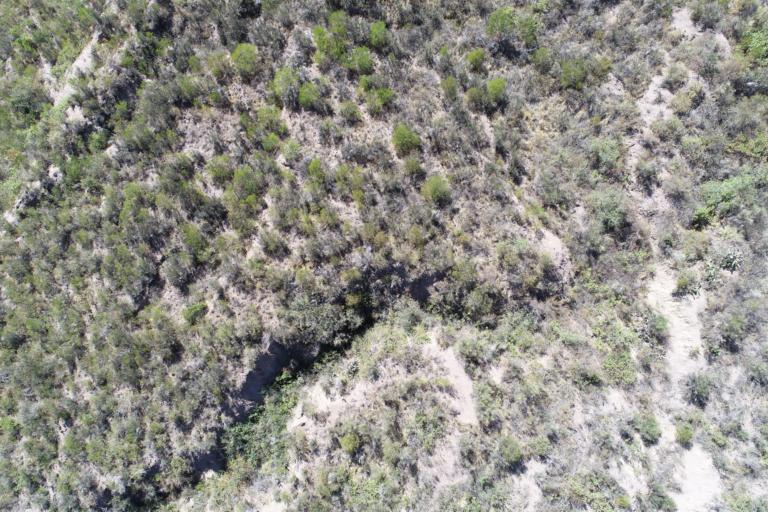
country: BO
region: La Paz
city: La Paz
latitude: -16.6213
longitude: -68.0382
